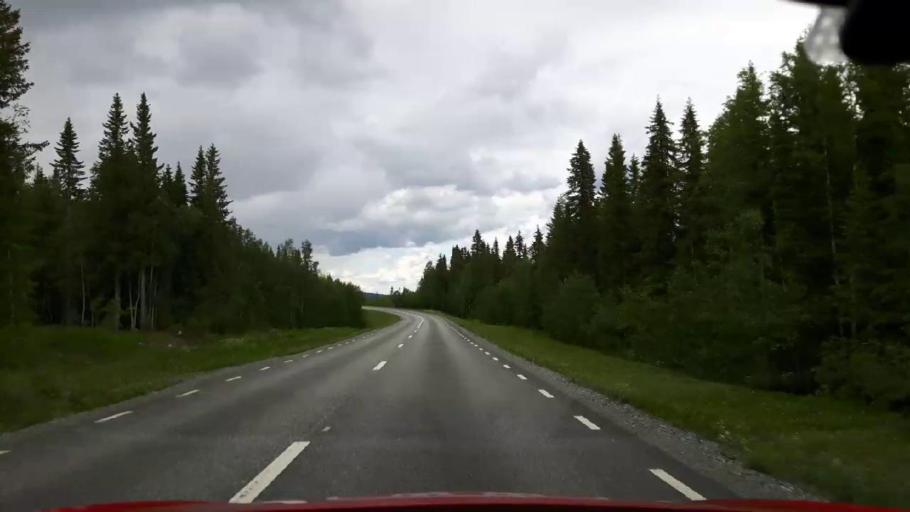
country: SE
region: Jaemtland
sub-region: Krokoms Kommun
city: Krokom
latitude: 63.6980
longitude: 14.3192
